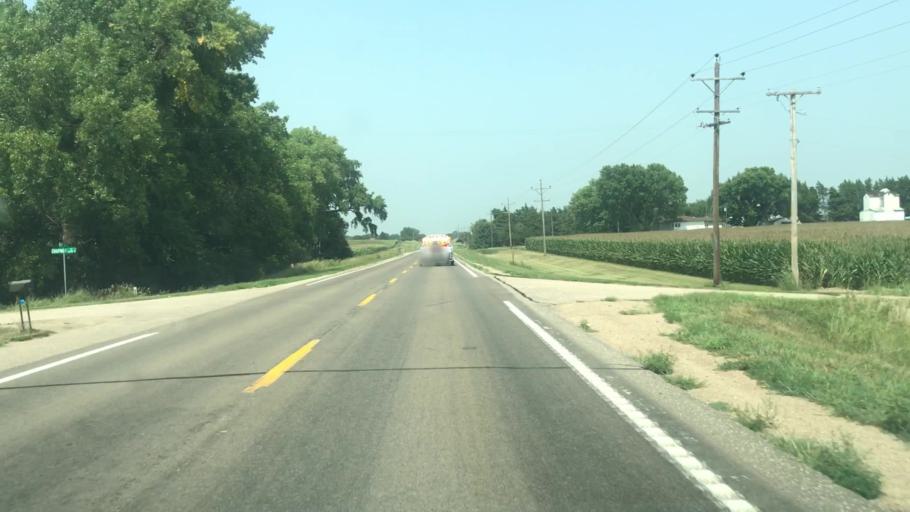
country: US
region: Nebraska
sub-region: Hall County
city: Wood River
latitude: 41.0182
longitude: -98.6074
